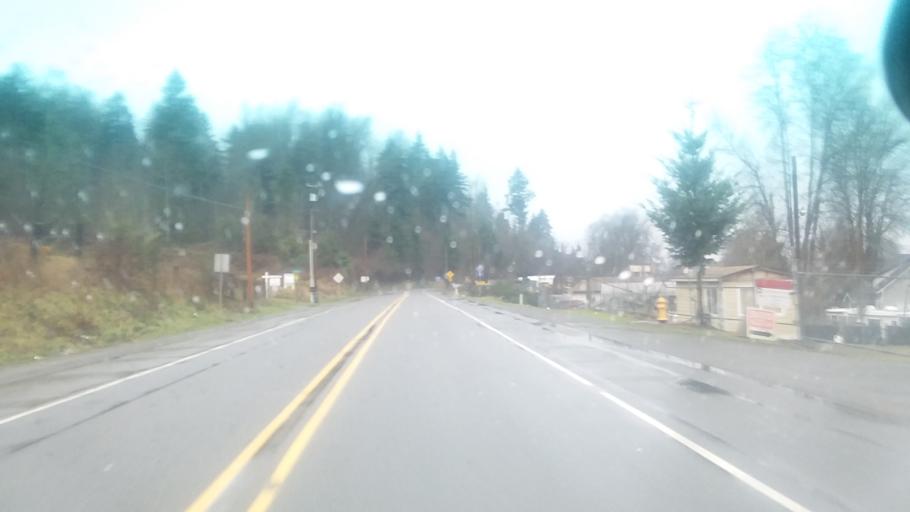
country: US
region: Washington
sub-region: King County
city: Pacific
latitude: 47.2415
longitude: -122.2560
